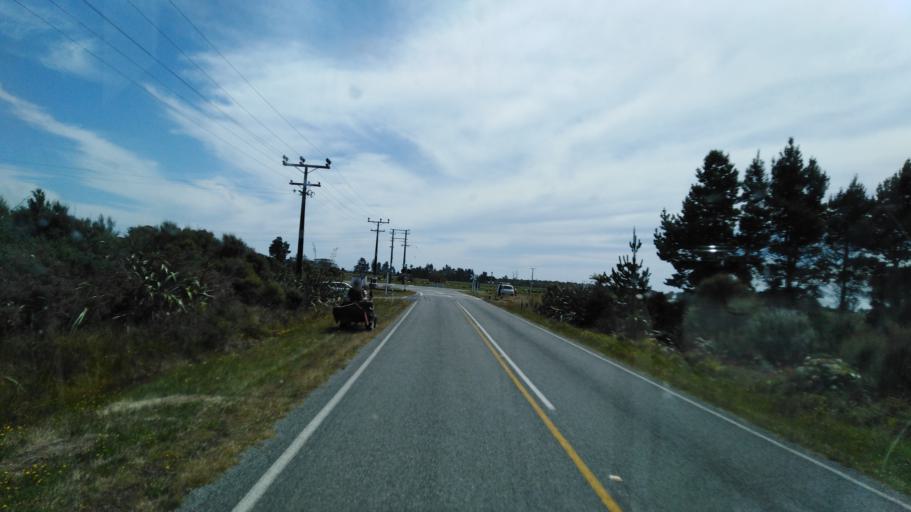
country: NZ
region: West Coast
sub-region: Buller District
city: Westport
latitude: -41.7380
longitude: 171.7064
